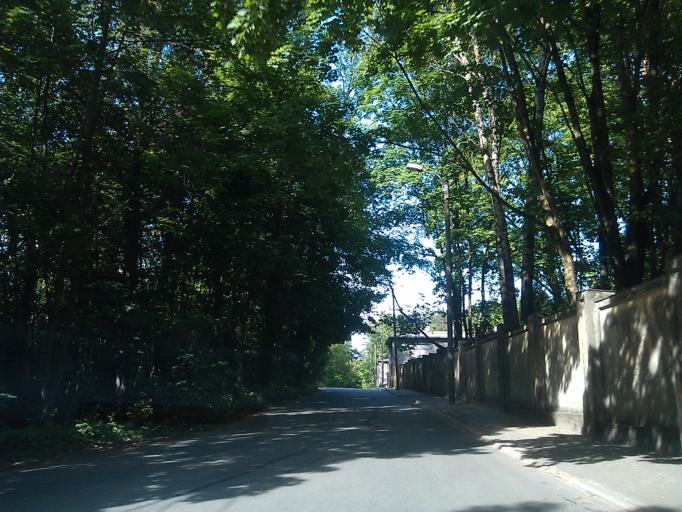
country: LV
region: Riga
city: Jaunciems
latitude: 56.9881
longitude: 24.2056
